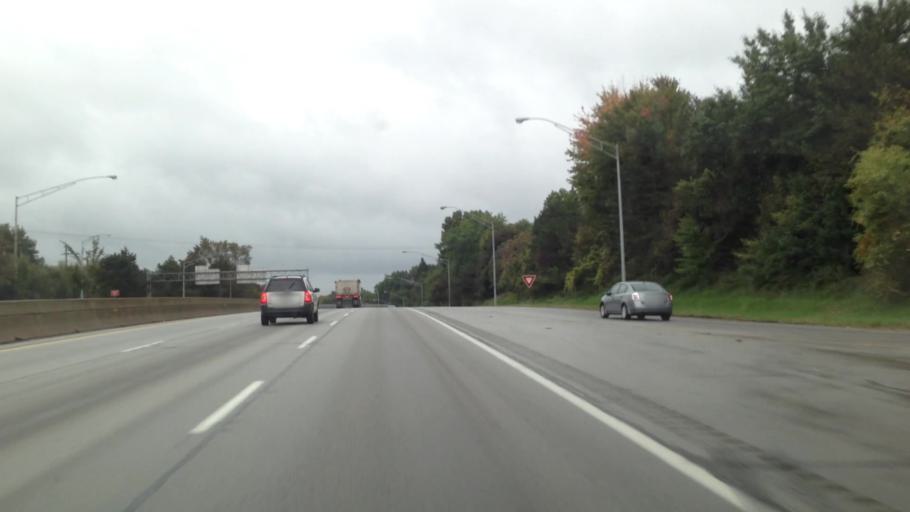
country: US
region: Ohio
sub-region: Summit County
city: Akron
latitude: 41.1012
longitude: -81.5002
